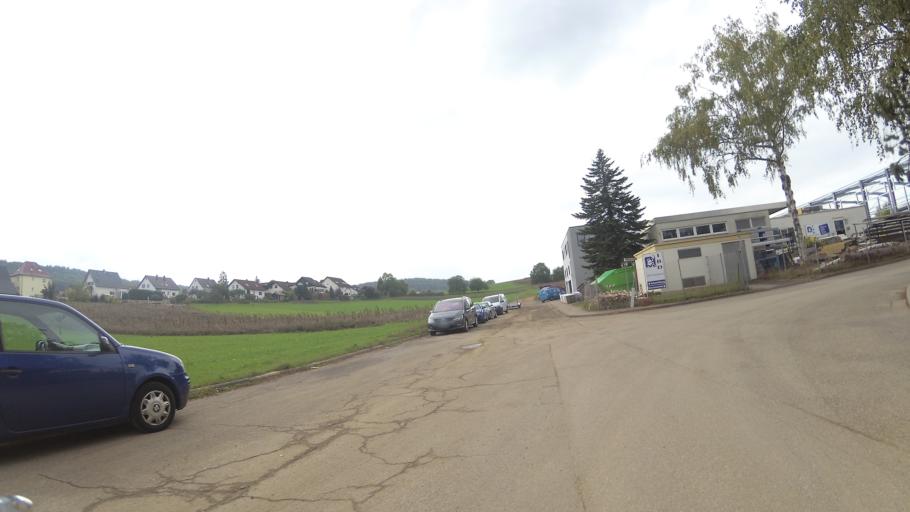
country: DE
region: Baden-Wuerttemberg
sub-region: Regierungsbezirk Stuttgart
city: Eberstadt
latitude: 49.2129
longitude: 9.2971
